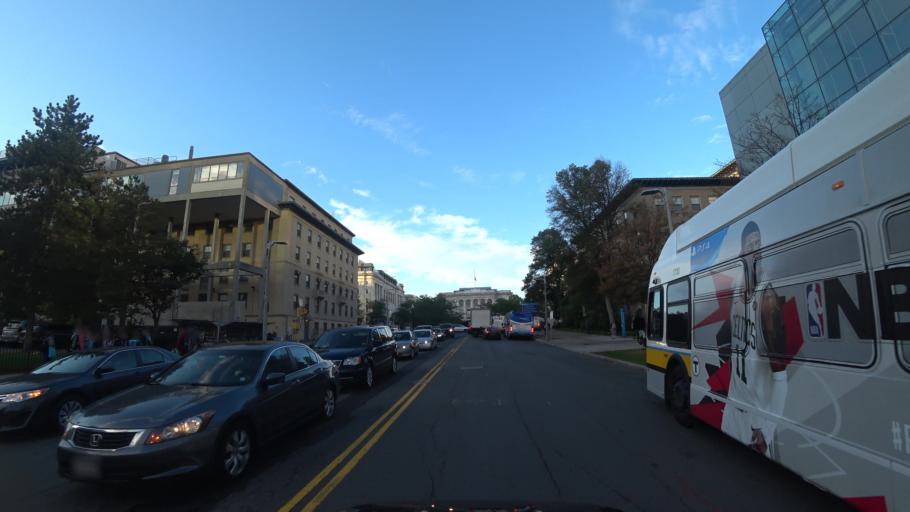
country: US
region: Massachusetts
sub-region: Norfolk County
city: Brookline
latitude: 42.3381
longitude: -71.1026
